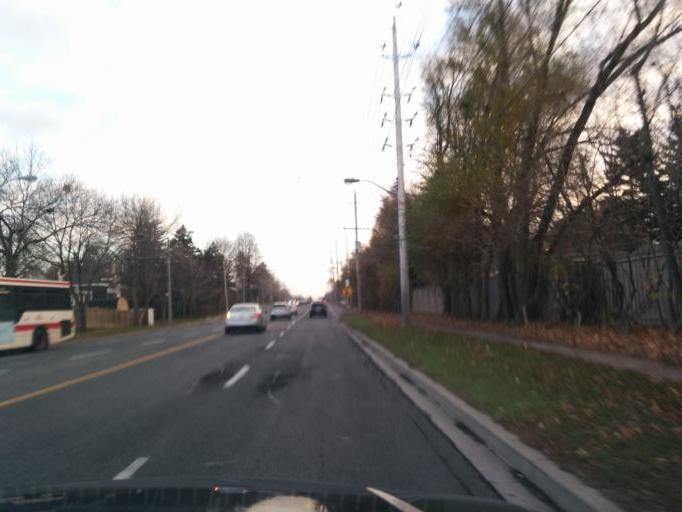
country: CA
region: Ontario
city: Etobicoke
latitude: 43.6829
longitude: -79.5404
